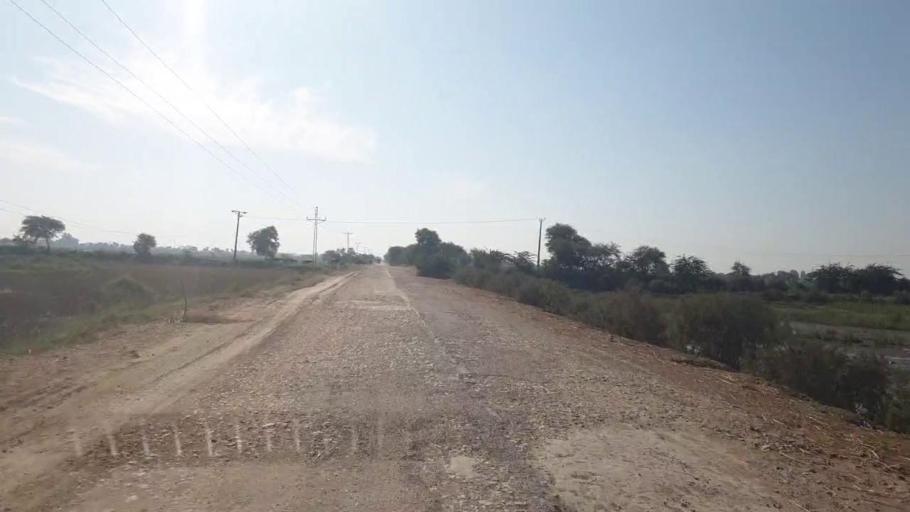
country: PK
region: Sindh
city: Talhar
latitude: 24.9107
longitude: 68.8191
